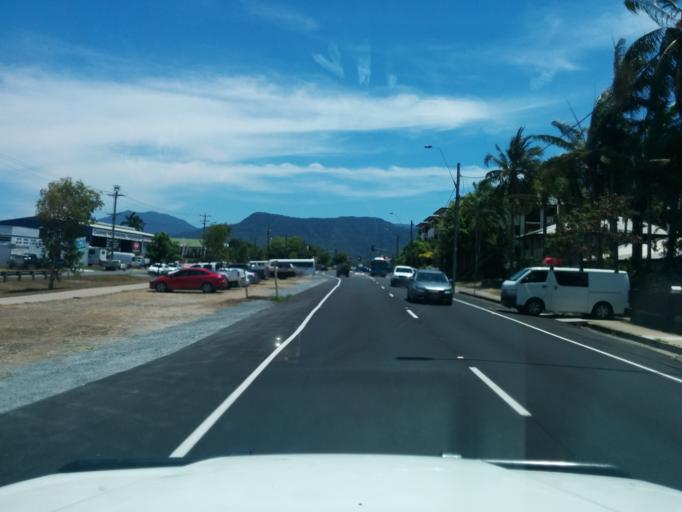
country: AU
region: Queensland
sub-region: Cairns
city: Cairns
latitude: -16.9328
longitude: 145.7657
